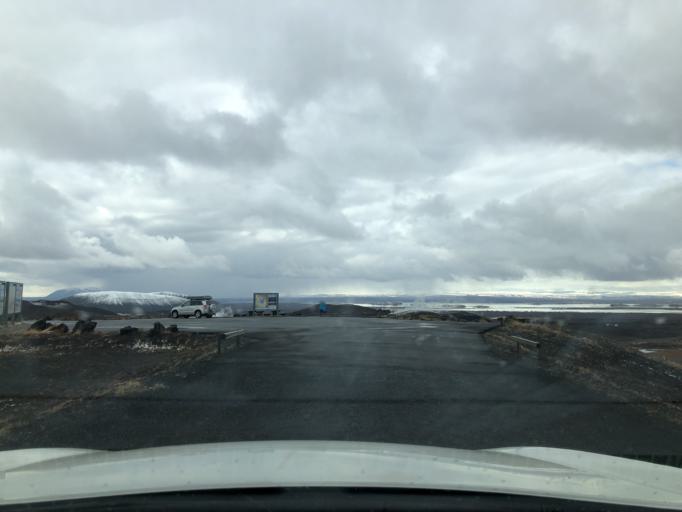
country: IS
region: Northeast
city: Laugar
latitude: 65.6424
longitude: -16.8325
